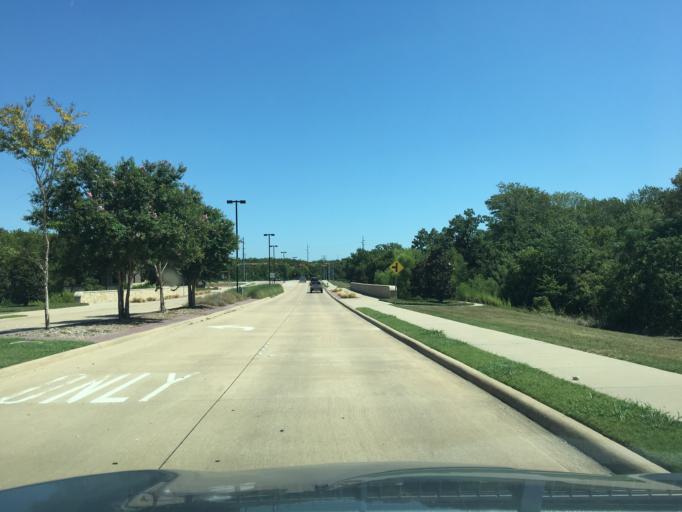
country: US
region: Texas
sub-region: Dallas County
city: Garland
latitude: 32.9561
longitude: -96.6343
